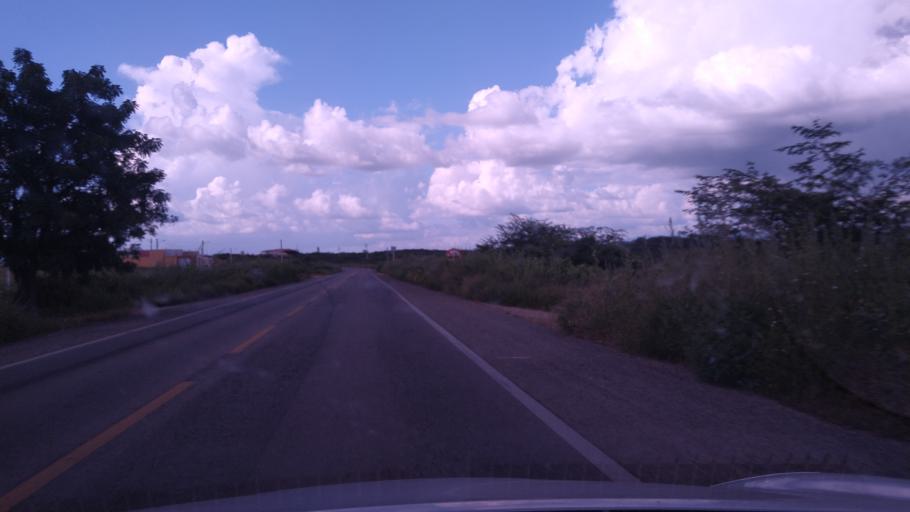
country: BR
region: Ceara
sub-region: Caninde
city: Caninde
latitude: -4.3971
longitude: -39.3165
